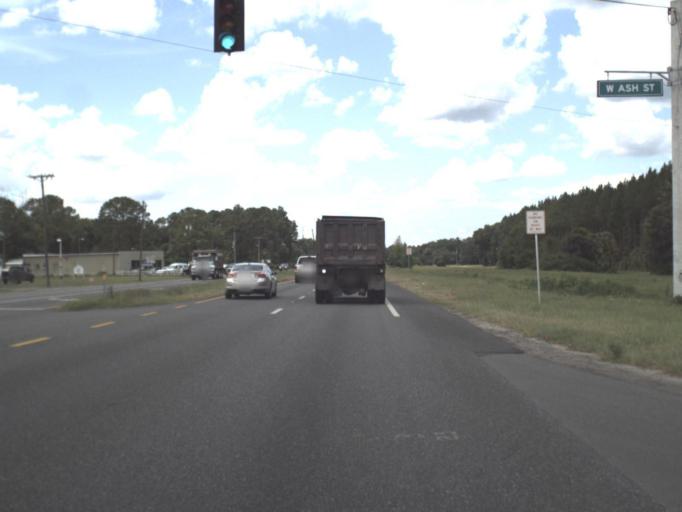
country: US
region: Florida
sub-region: Taylor County
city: Perry
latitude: 30.1279
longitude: -83.5971
